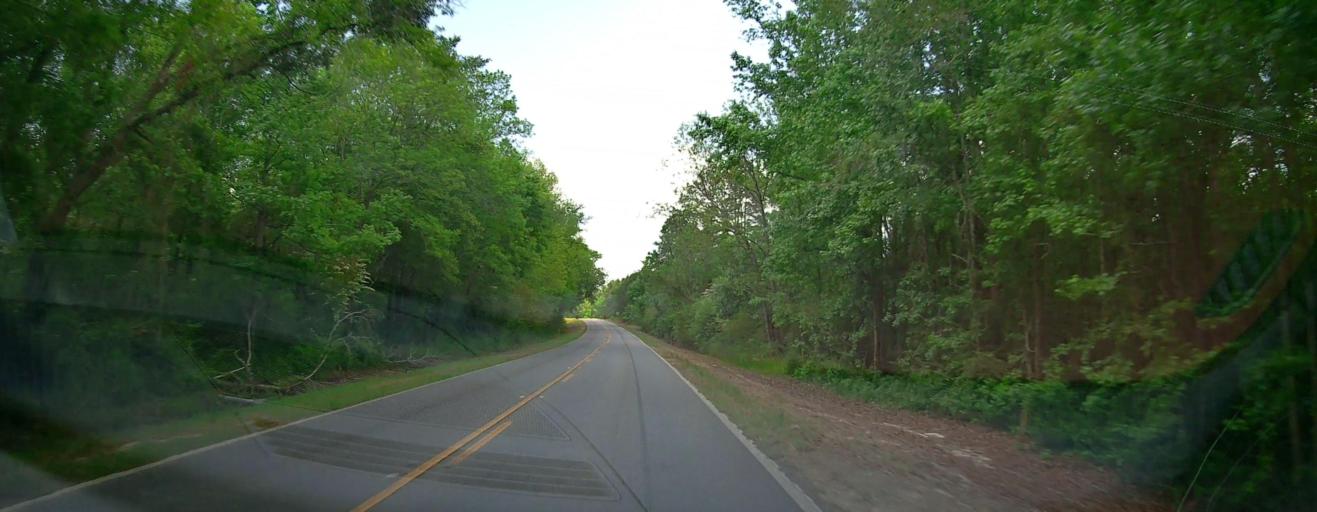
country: US
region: Georgia
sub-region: Treutlen County
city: Soperton
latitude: 32.5180
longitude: -82.6628
